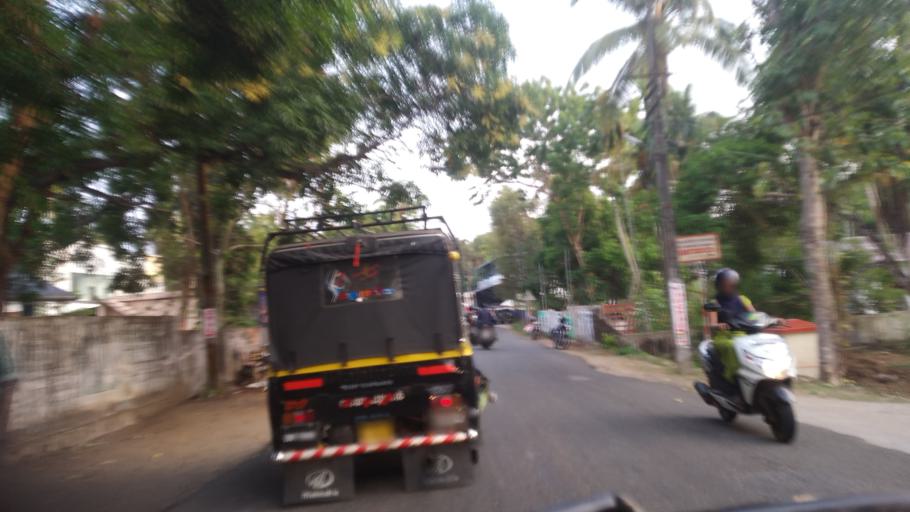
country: IN
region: Kerala
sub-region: Thrissur District
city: Kodungallur
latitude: 10.2397
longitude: 76.1519
